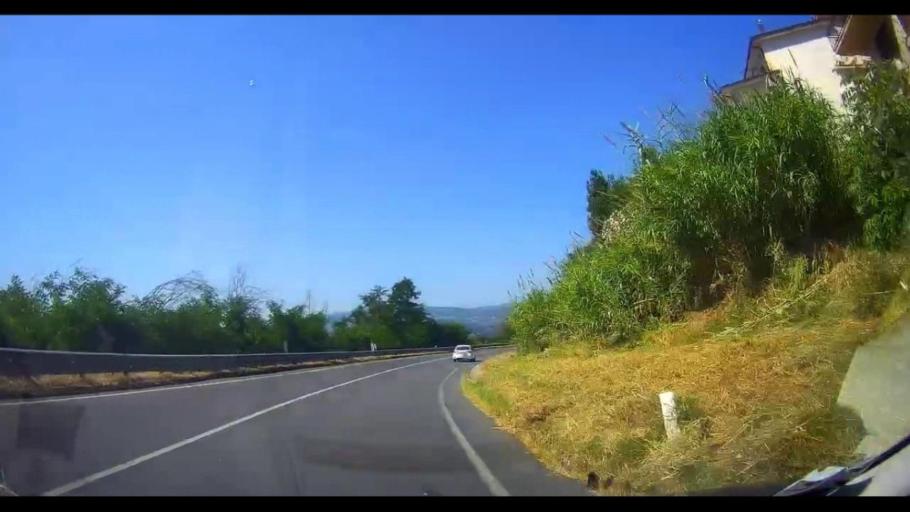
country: IT
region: Calabria
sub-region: Provincia di Cosenza
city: Rovito
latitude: 39.3010
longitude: 16.3137
